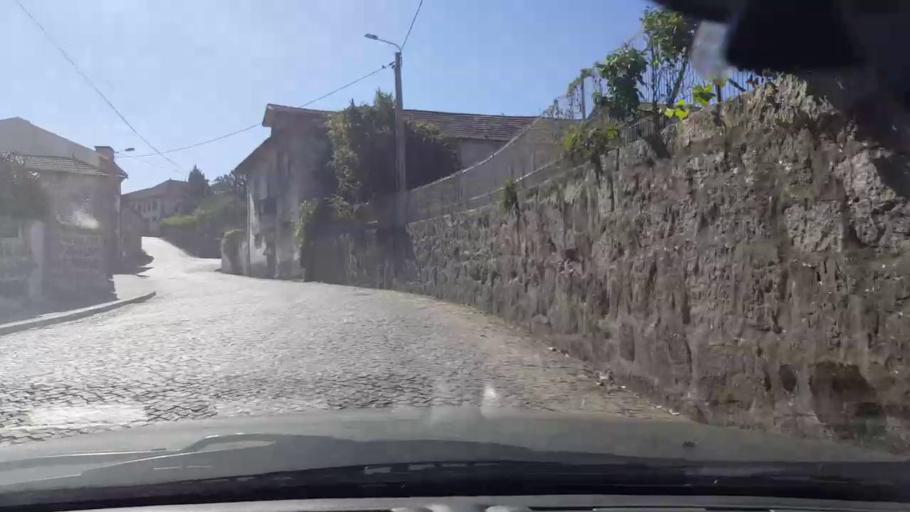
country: PT
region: Porto
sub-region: Maia
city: Gemunde
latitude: 41.2777
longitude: -8.6711
